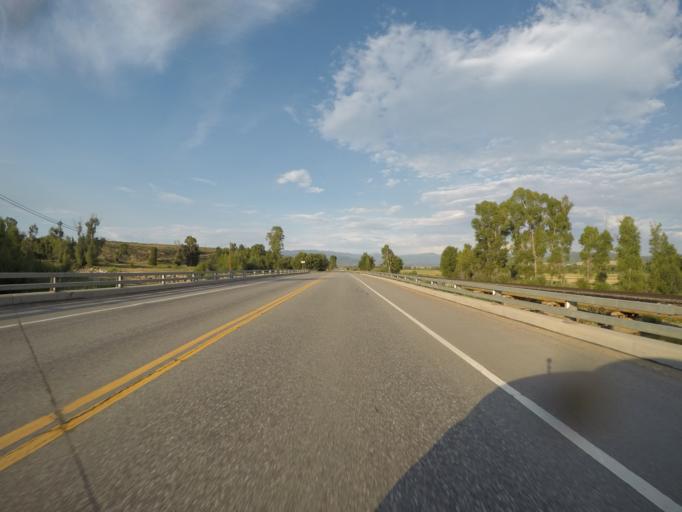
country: US
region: Colorado
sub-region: Routt County
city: Steamboat Springs
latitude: 40.4868
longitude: -106.9688
